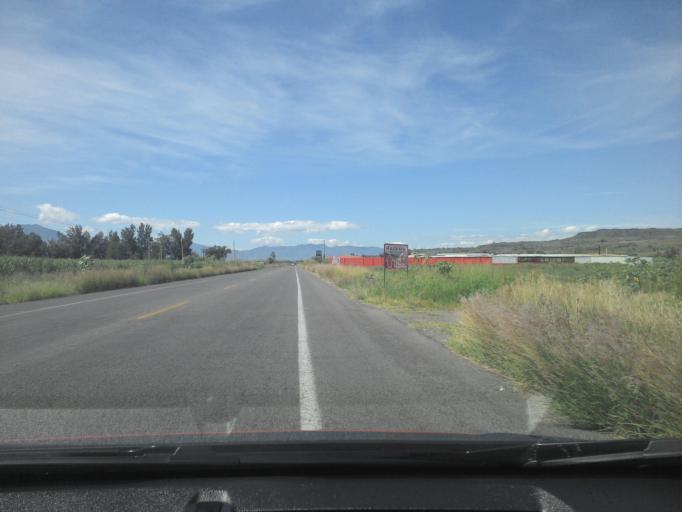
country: MX
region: Jalisco
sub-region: Teuchitlan
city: La Estanzuela
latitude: 20.6682
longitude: -103.7960
